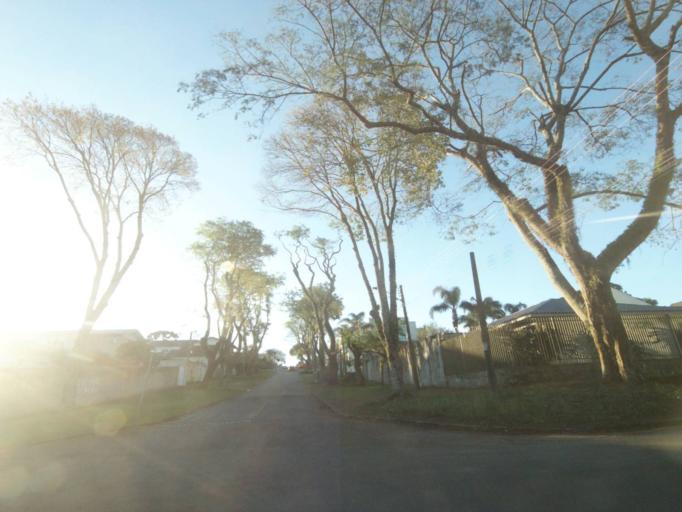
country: BR
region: Parana
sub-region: Curitiba
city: Curitiba
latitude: -25.3913
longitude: -49.2492
